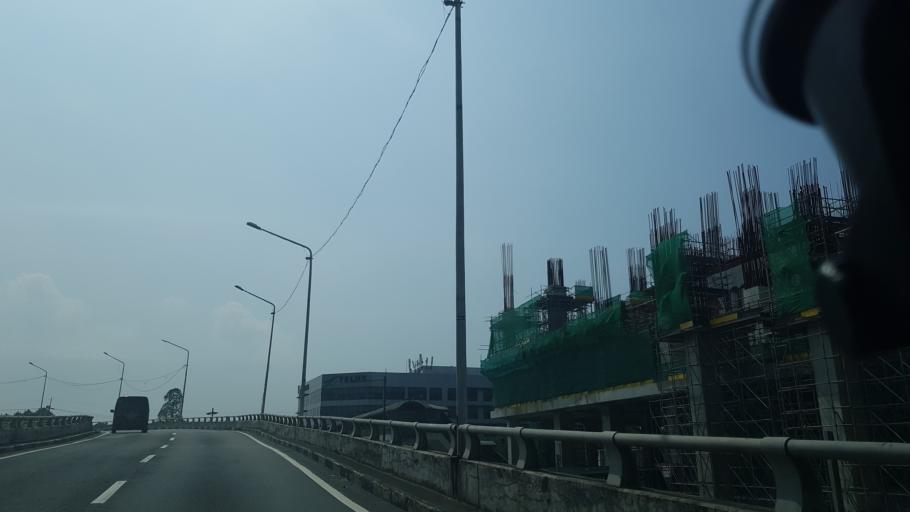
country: PH
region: Metro Manila
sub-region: Makati City
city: Makati City
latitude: 14.5511
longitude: 121.0288
